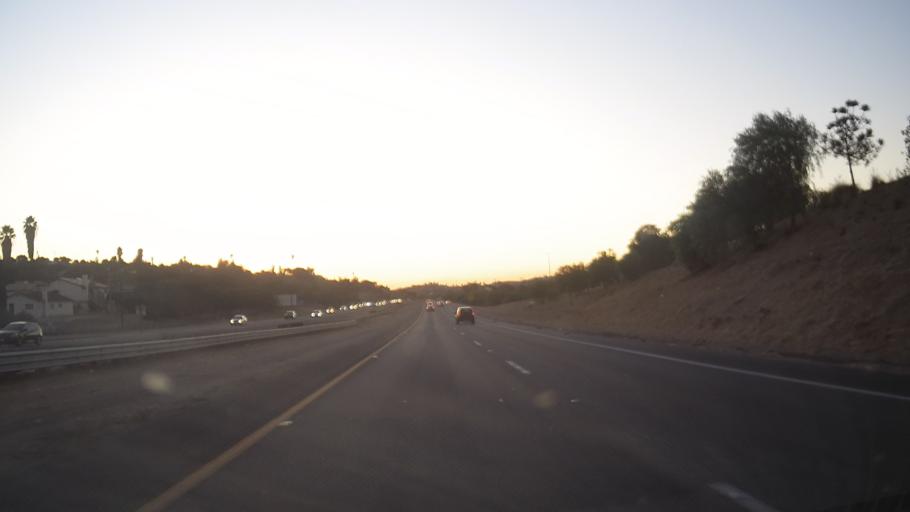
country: US
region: California
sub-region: San Diego County
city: Casa de Oro-Mount Helix
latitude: 32.7449
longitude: -116.9748
